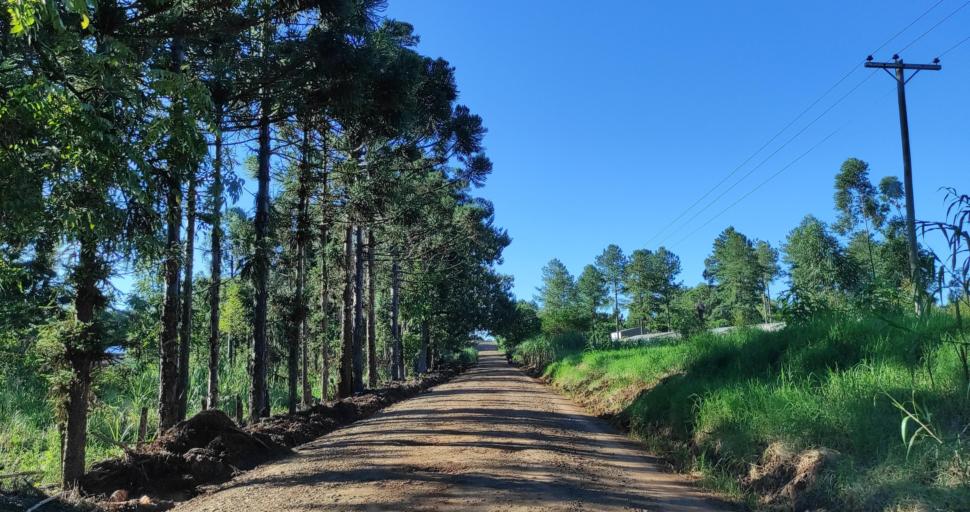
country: AR
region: Misiones
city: Puerto Rico
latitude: -26.8272
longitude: -55.0011
